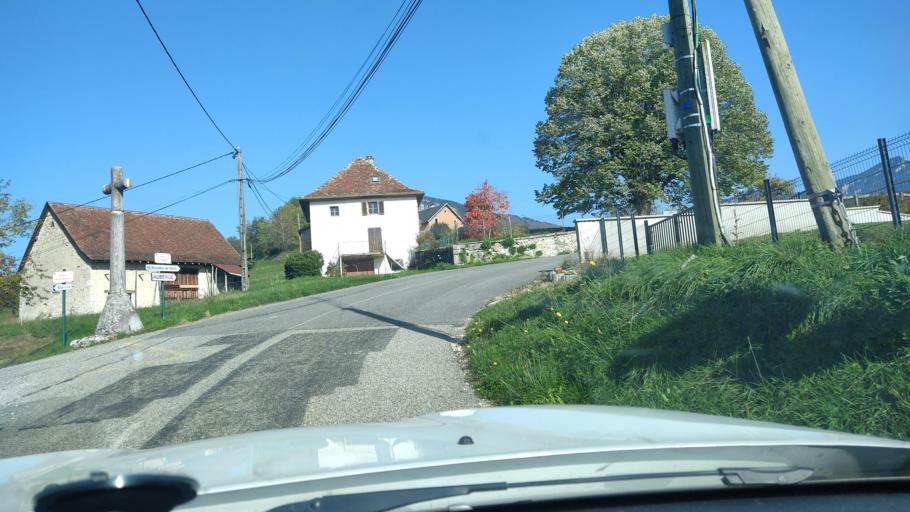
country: FR
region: Rhone-Alpes
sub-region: Departement de la Savoie
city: Les Echelles
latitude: 45.4524
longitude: 5.7545
